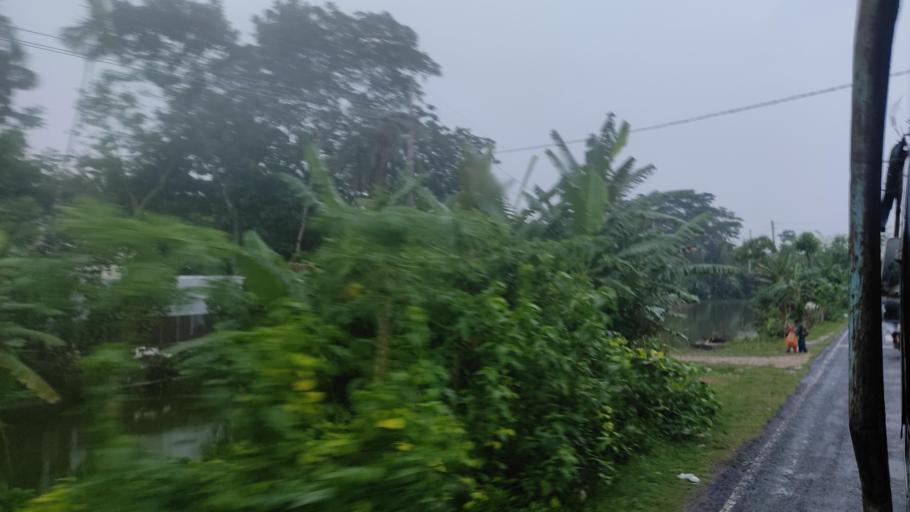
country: BD
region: Barisal
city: Bhandaria
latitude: 22.2979
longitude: 90.3246
